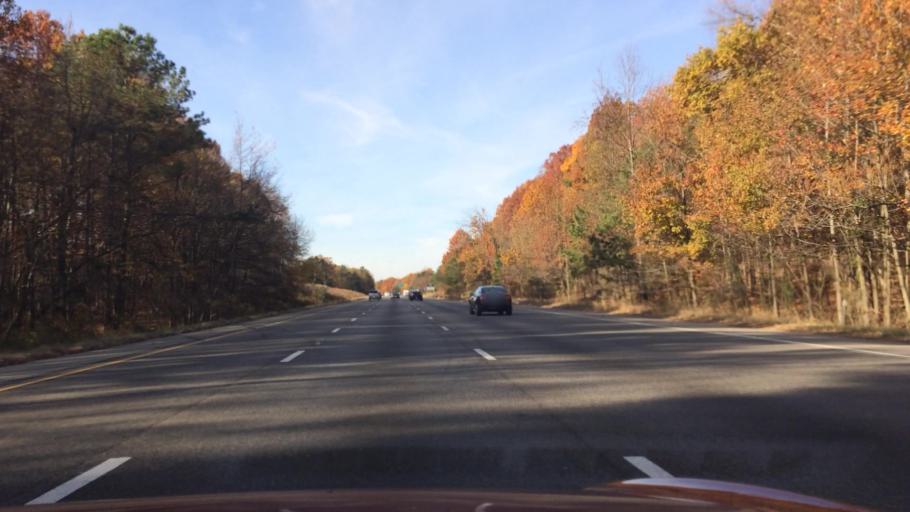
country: US
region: Virginia
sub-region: Henrico County
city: Glen Allen
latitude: 37.6796
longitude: -77.5484
